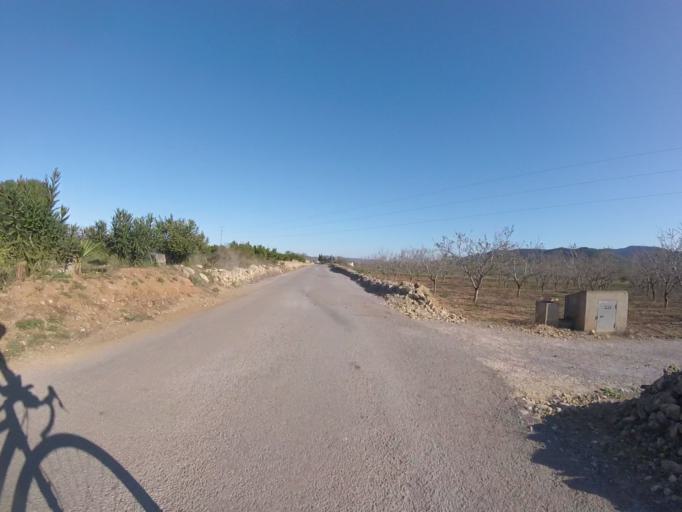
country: ES
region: Valencia
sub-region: Provincia de Castello
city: Alcala de Xivert
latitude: 40.2895
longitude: 0.2157
